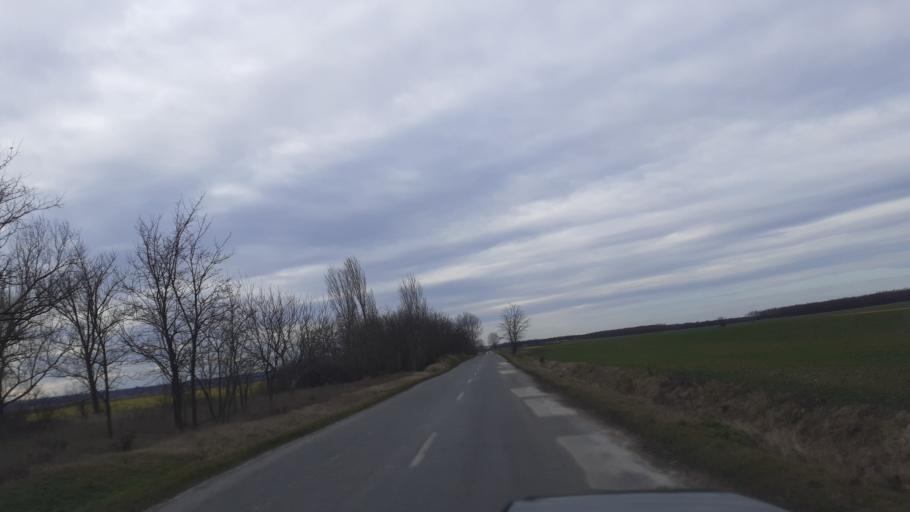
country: HU
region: Fejer
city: Sarbogard
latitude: 46.9078
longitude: 18.5848
